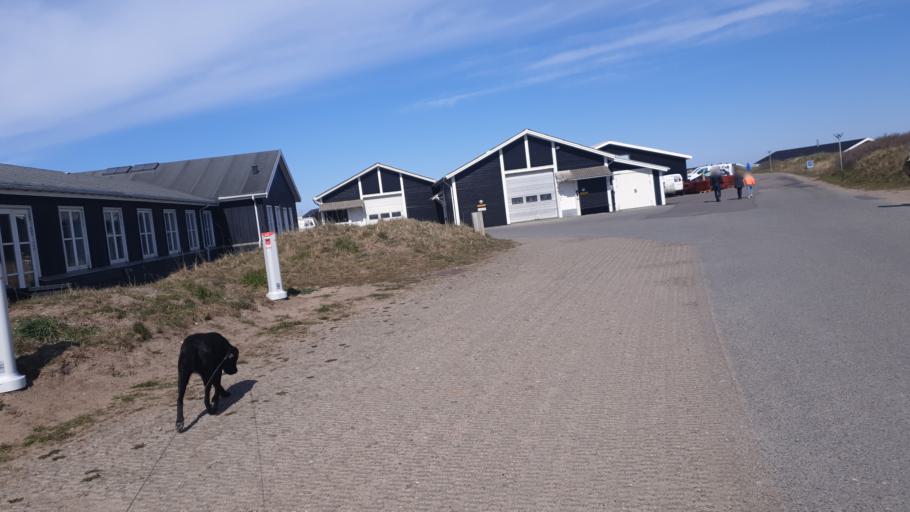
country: DK
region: North Denmark
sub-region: Hjorring Kommune
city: Hjorring
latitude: 57.4952
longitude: 9.8380
